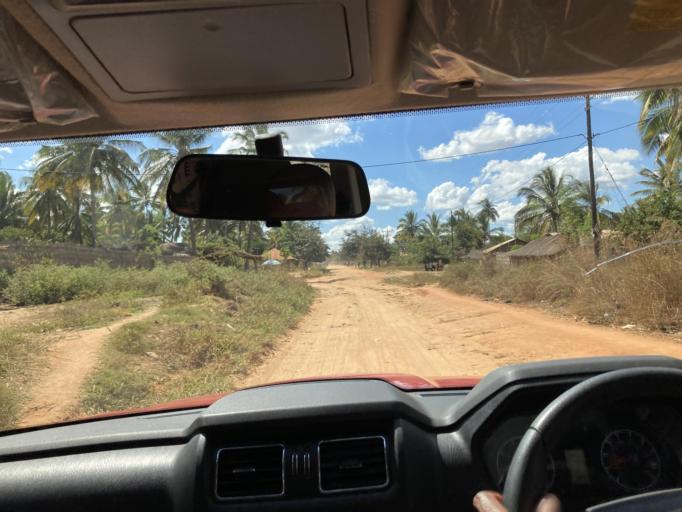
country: MZ
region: Cabo Delgado
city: Montepuez
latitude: -13.1441
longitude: 38.9933
